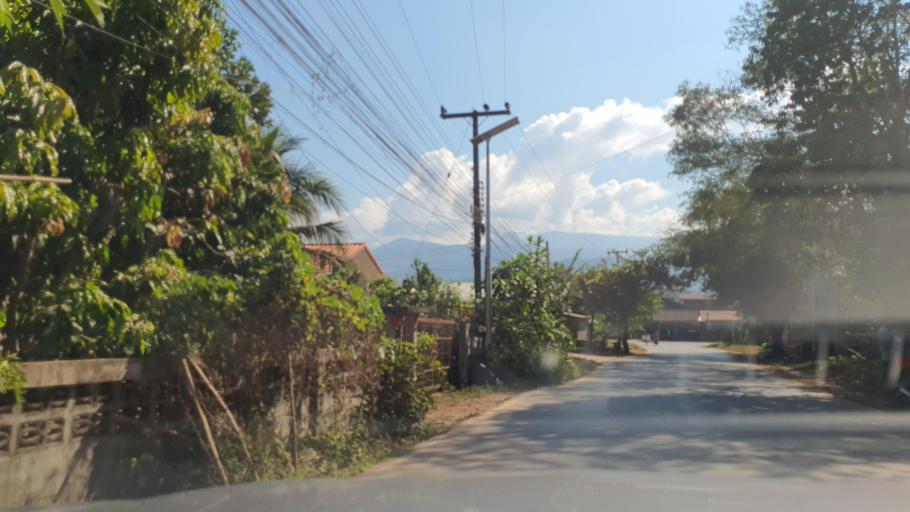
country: TH
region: Nan
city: Pua
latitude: 19.1406
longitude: 100.9331
